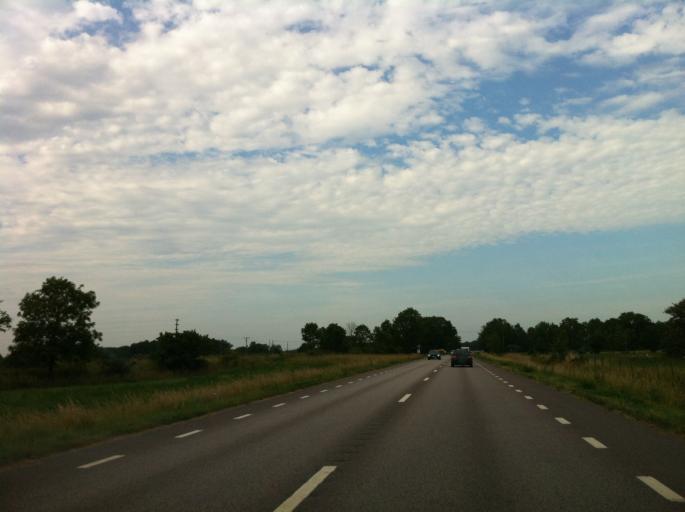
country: SE
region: Kalmar
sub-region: Borgholms Kommun
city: Borgholm
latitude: 56.9865
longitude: 16.8133
